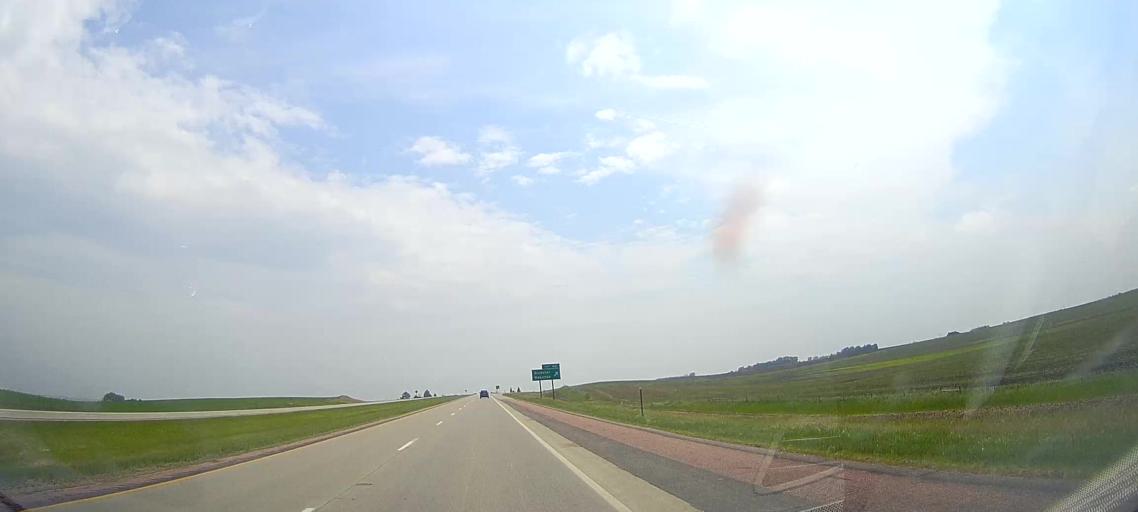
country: US
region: South Dakota
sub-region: Union County
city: Beresford
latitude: 43.0165
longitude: -96.7958
